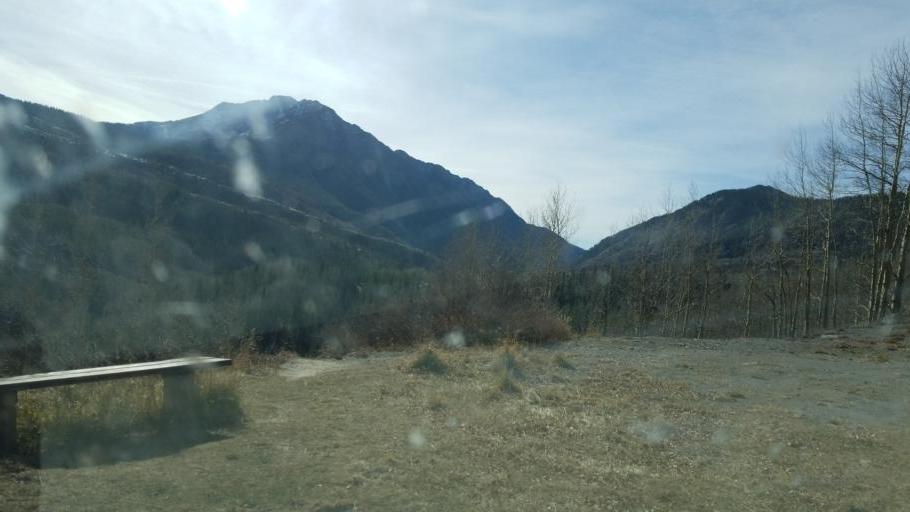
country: US
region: Colorado
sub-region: San Juan County
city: Silverton
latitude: 37.7154
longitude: -107.7545
